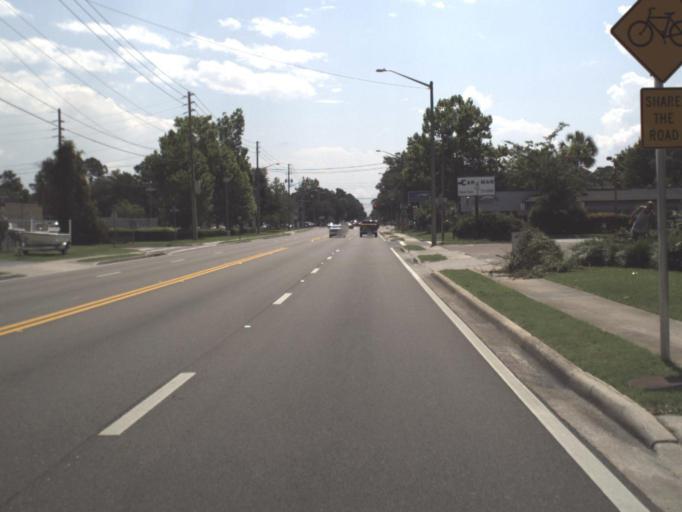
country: US
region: Florida
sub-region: Alachua County
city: Gainesville
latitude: 29.6739
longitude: -82.3245
